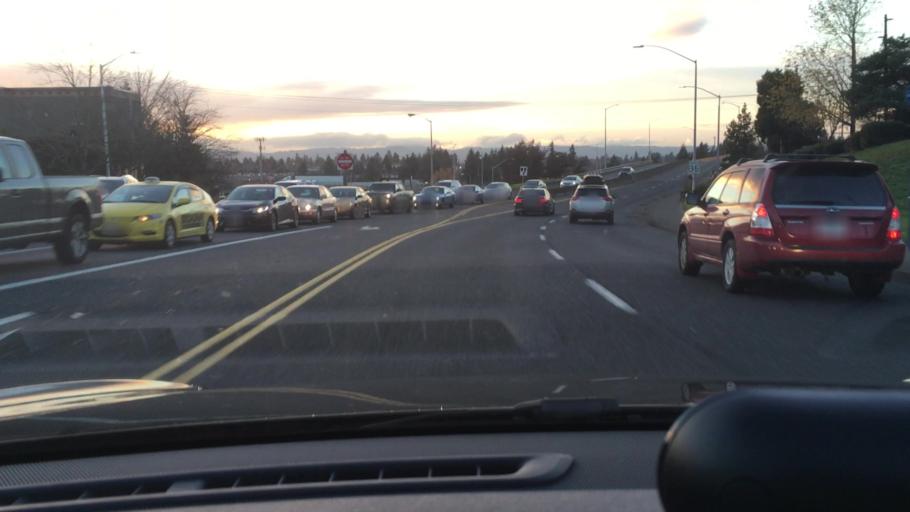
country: US
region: Oregon
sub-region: Multnomah County
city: Lents
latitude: 45.5336
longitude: -122.5611
